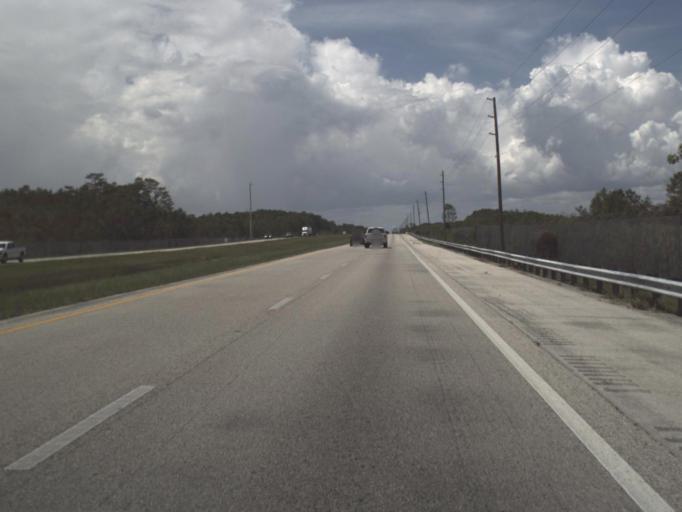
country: US
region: Florida
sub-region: Collier County
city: Immokalee
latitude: 26.1681
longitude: -81.1316
